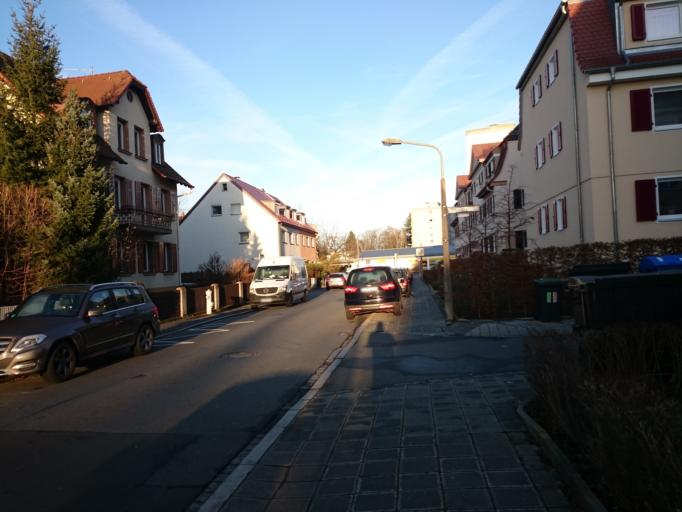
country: DE
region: Bavaria
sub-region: Regierungsbezirk Mittelfranken
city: Nuernberg
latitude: 49.4442
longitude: 11.1288
